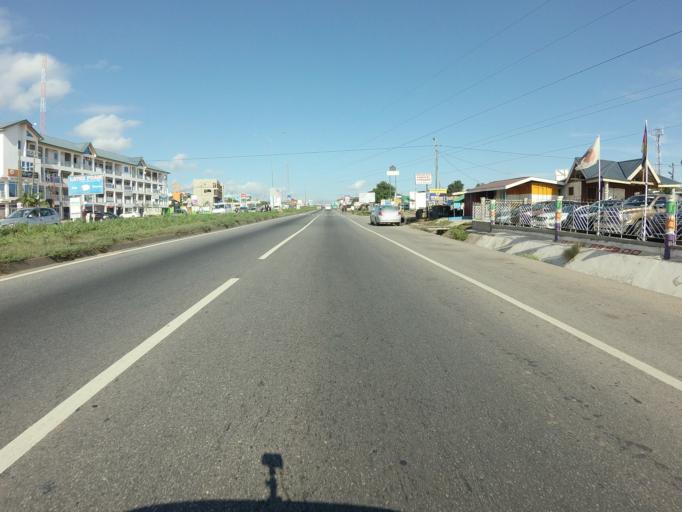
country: GH
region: Greater Accra
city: Gbawe
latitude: 5.5495
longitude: -0.3522
